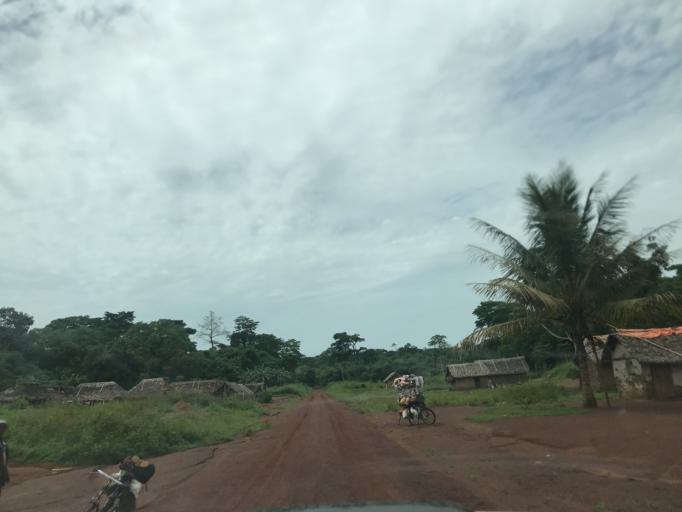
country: CD
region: Eastern Province
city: Buta
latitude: 2.4079
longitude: 24.9098
